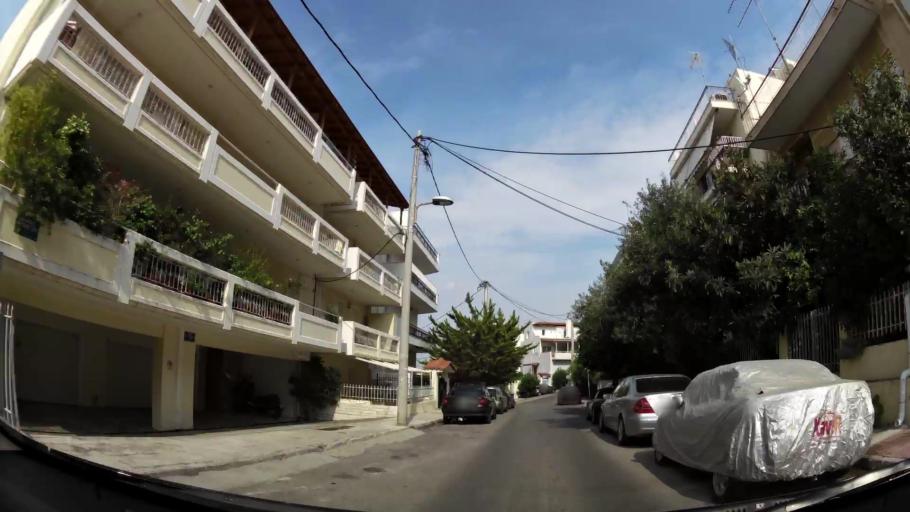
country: GR
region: Attica
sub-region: Nomarchia Athinas
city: Galatsi
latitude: 38.0048
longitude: 23.7516
